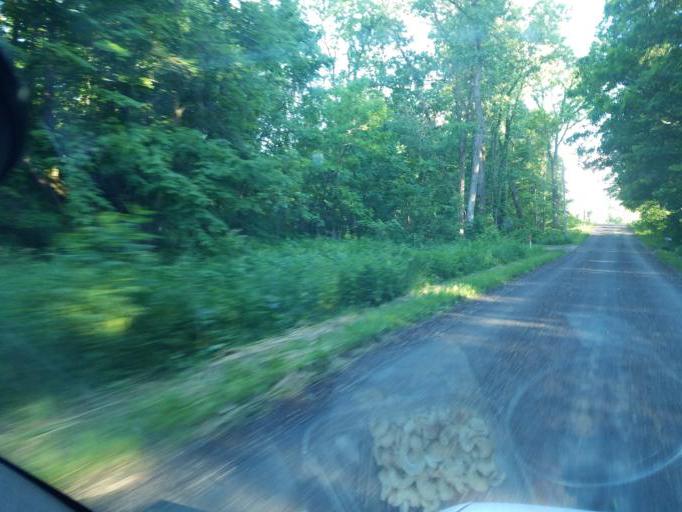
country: US
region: Ohio
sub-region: Morrow County
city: Mount Gilead
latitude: 40.4689
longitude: -82.7236
